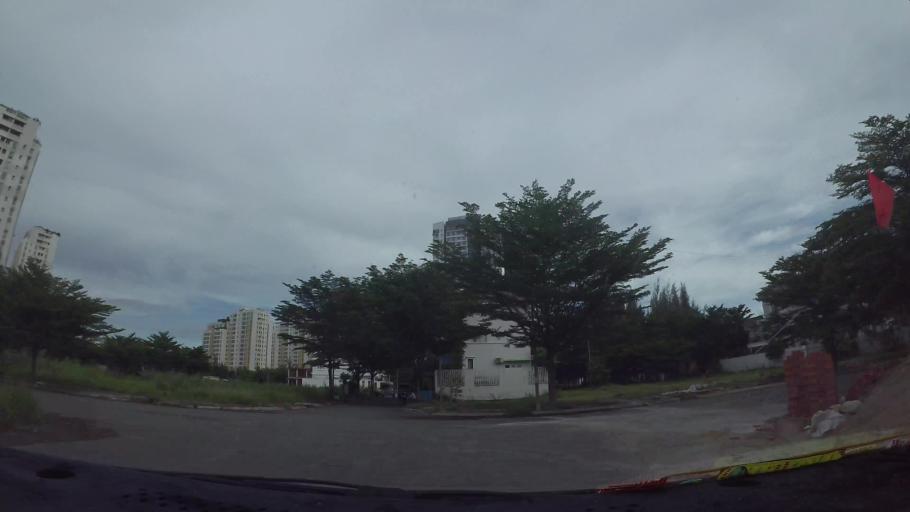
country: VN
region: Ho Chi Minh City
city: Quan Sau
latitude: 10.7466
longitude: 106.6565
